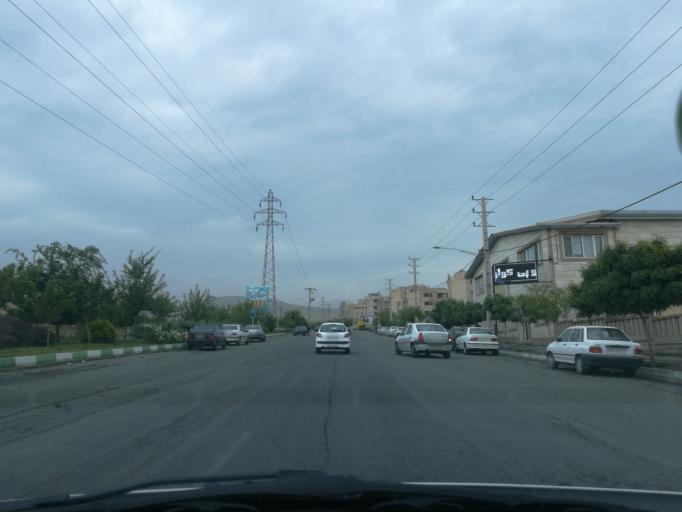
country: IR
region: Alborz
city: Karaj
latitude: 35.8617
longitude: 50.9254
